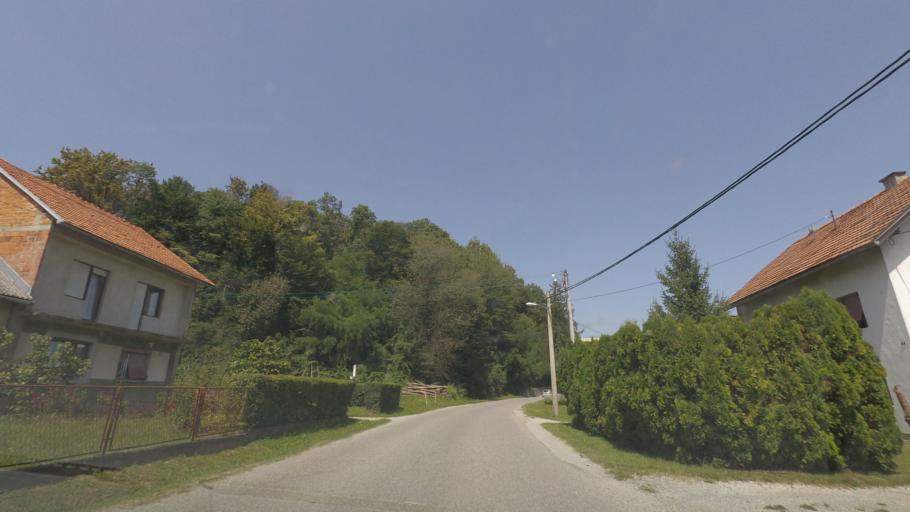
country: HR
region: Karlovacka
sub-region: Grad Karlovac
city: Karlovac
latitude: 45.5080
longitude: 15.5190
